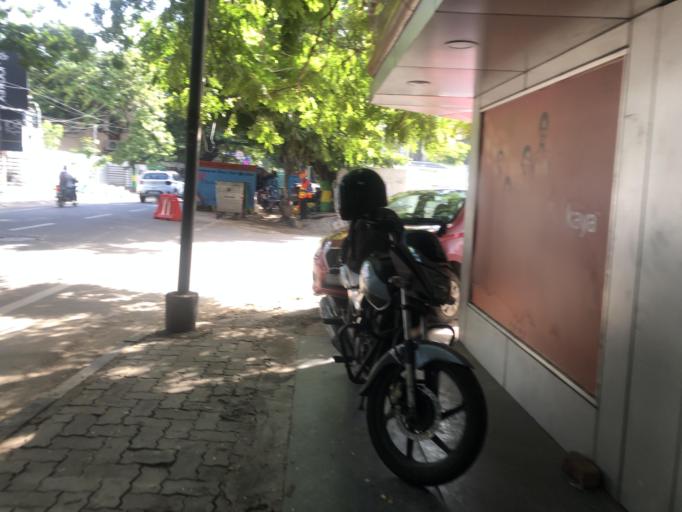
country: IN
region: Tamil Nadu
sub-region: Chennai
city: Gandhi Nagar
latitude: 13.0358
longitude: 80.2551
